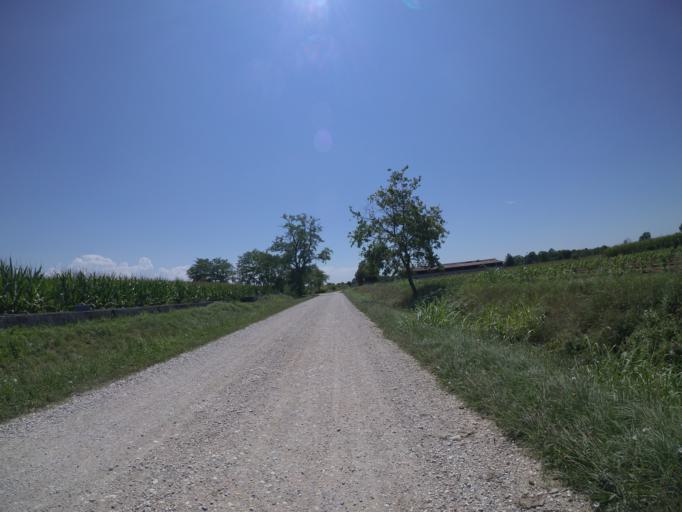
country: IT
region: Friuli Venezia Giulia
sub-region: Provincia di Udine
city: Talmassons
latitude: 45.9247
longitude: 13.1035
